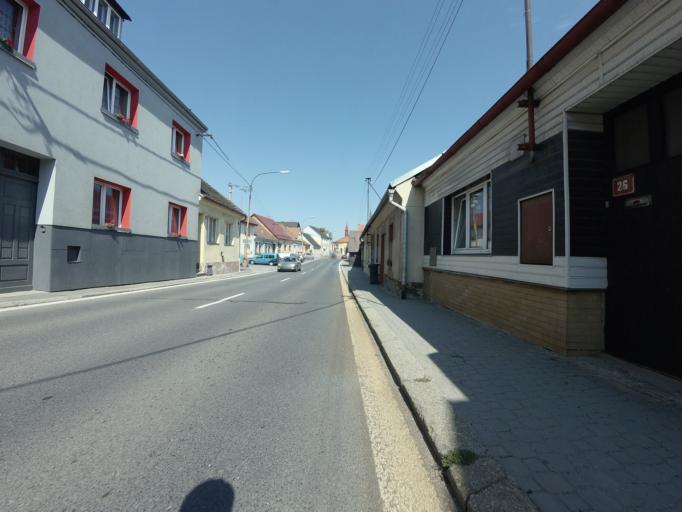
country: CZ
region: Jihocesky
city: Milevsko
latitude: 49.4478
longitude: 14.3602
